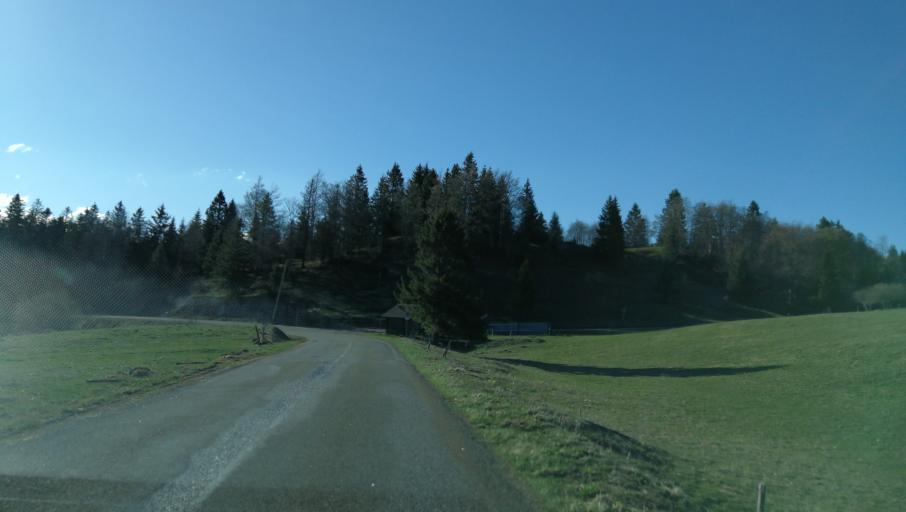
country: FR
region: Franche-Comte
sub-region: Departement du Jura
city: Saint-Claude
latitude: 46.2784
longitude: 5.8338
